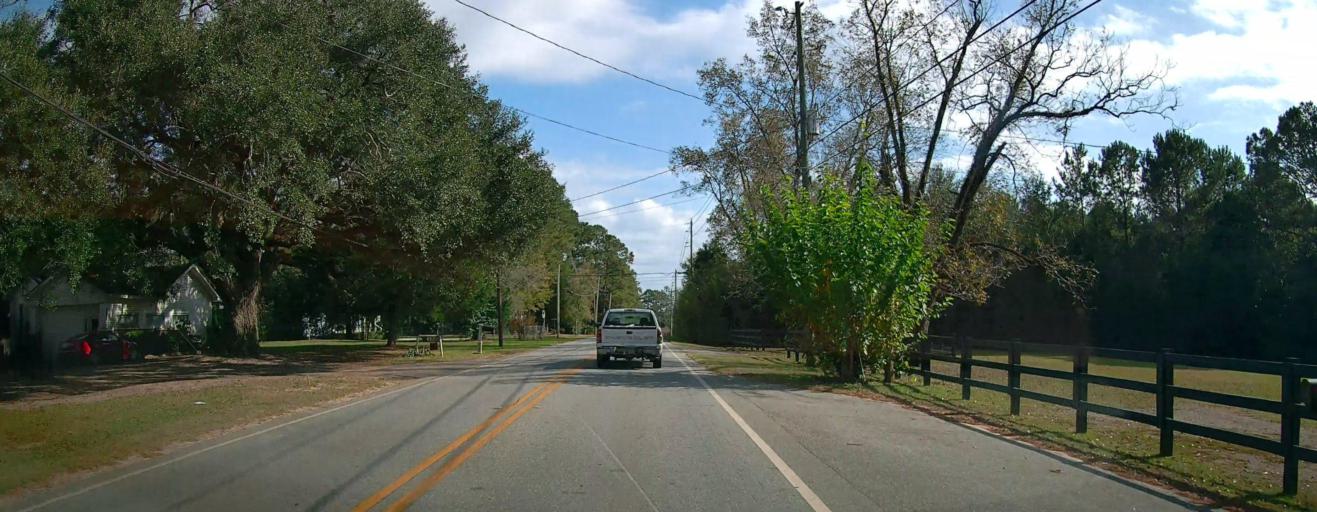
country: US
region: Georgia
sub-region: Thomas County
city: Thomasville
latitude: 30.8740
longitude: -84.0043
